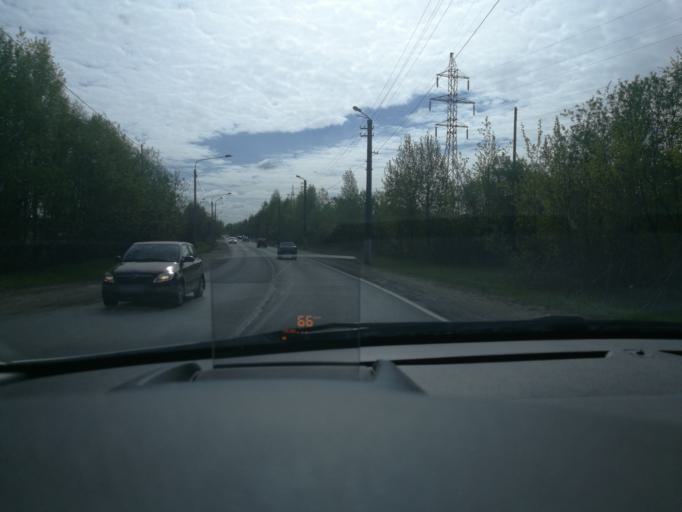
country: RU
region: Arkhangelskaya
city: Arkhangel'sk
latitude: 64.5983
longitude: 40.5572
